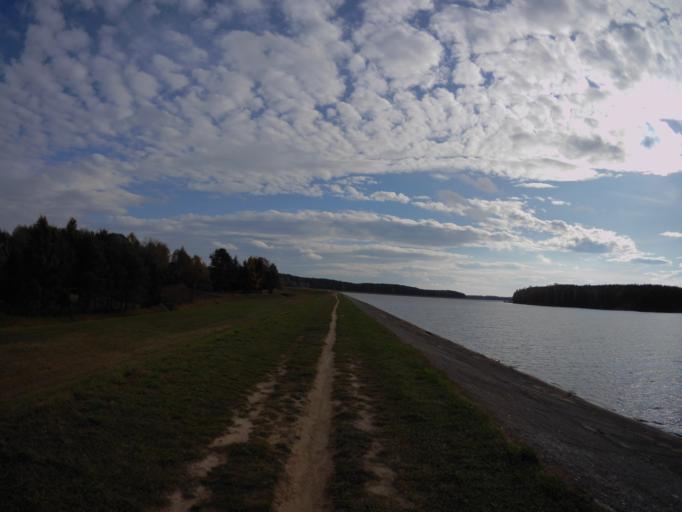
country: PL
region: Subcarpathian Voivodeship
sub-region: Powiat kolbuszowski
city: Lipnica
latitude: 50.3405
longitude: 21.9358
